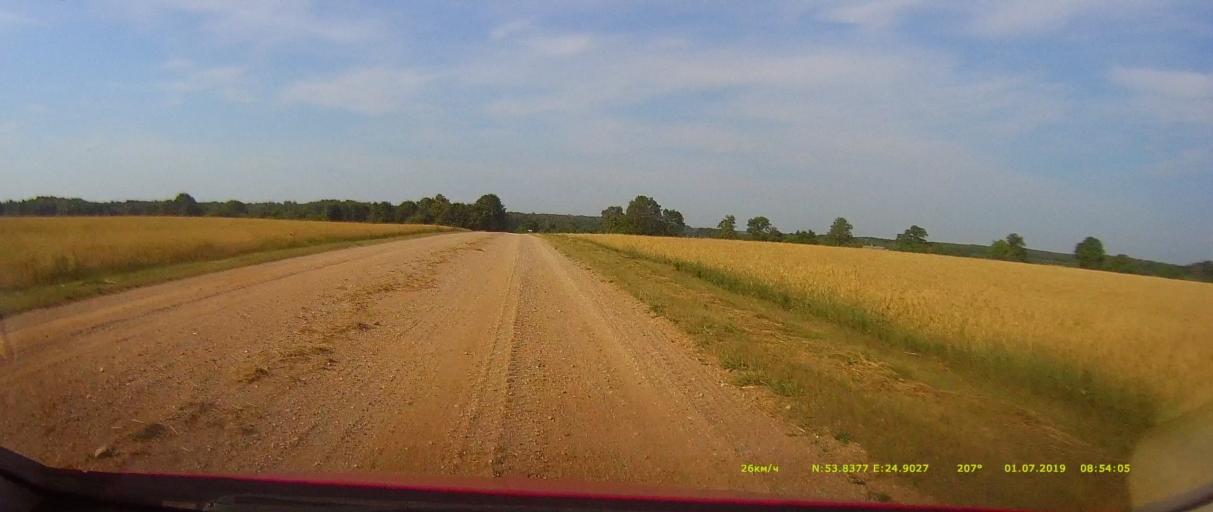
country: BY
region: Grodnenskaya
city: Shchuchin
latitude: 53.8378
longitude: 24.9027
